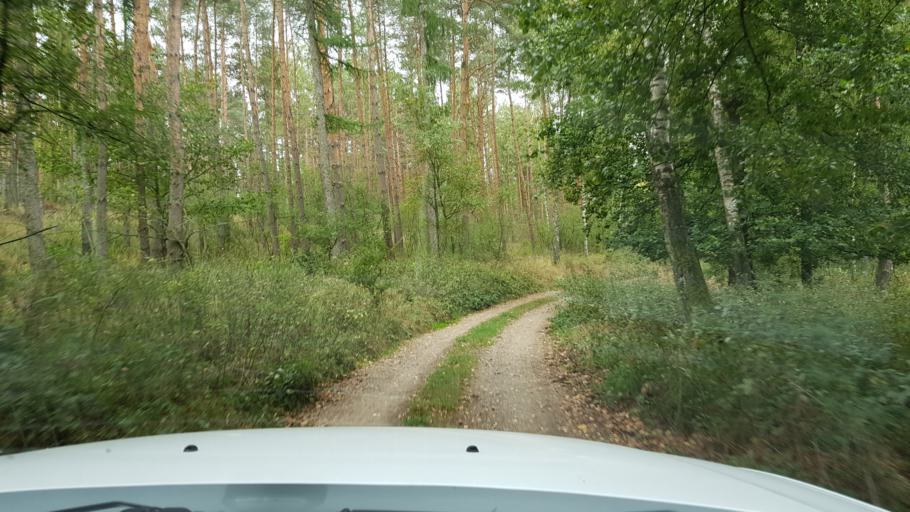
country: PL
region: West Pomeranian Voivodeship
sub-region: Powiat gryfinski
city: Cedynia
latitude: 52.8397
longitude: 14.2767
